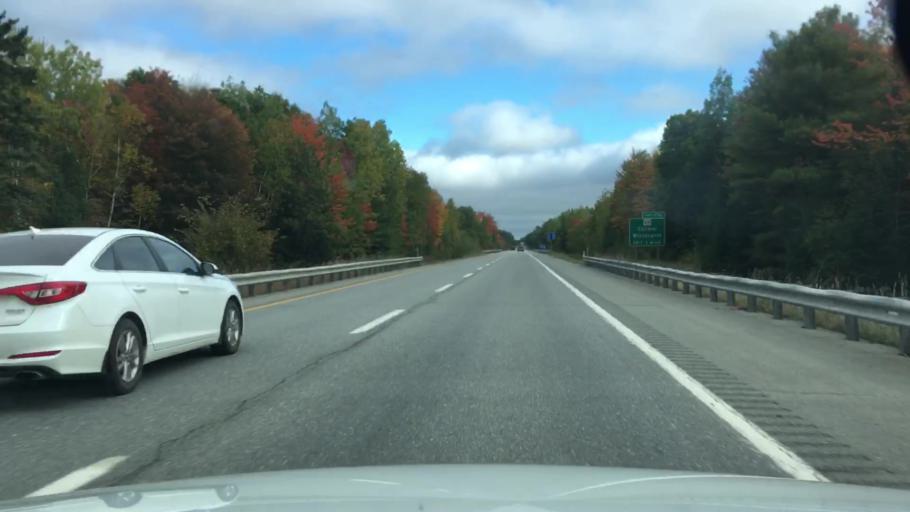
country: US
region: Maine
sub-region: Penobscot County
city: Carmel
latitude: 44.7678
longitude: -68.9971
